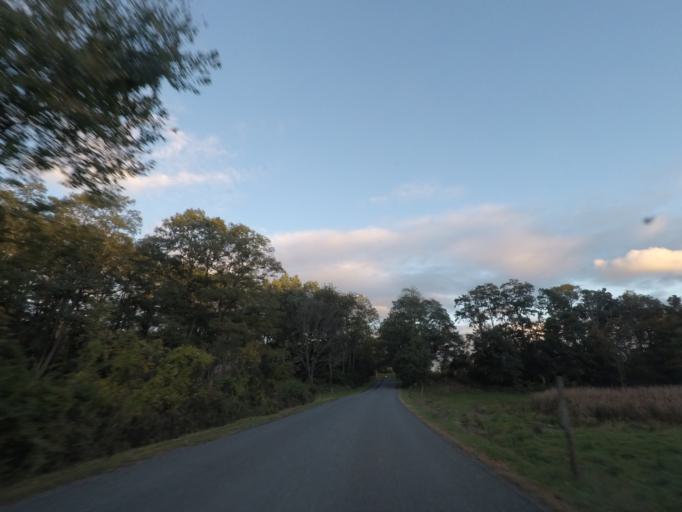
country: US
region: New York
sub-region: Rensselaer County
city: Nassau
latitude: 42.4918
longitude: -73.5762
